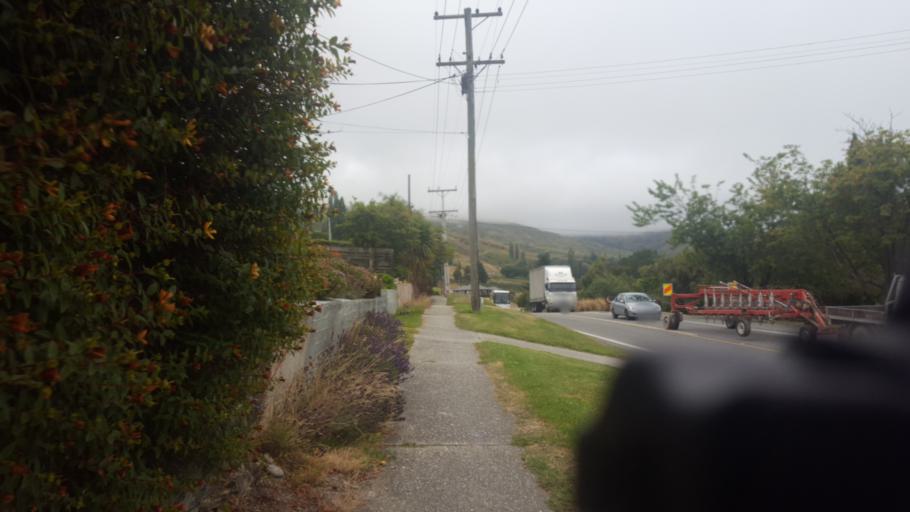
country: NZ
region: Otago
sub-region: Queenstown-Lakes District
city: Kingston
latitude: -45.5353
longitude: 169.3041
